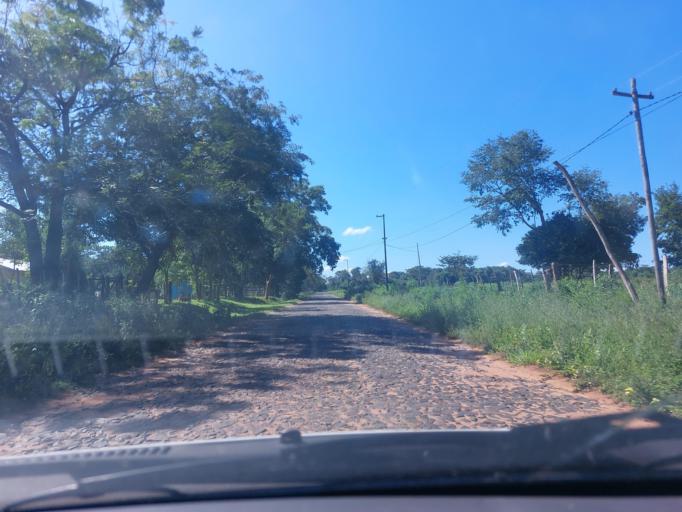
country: PY
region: San Pedro
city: Itacurubi del Rosario
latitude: -24.5769
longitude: -56.5998
